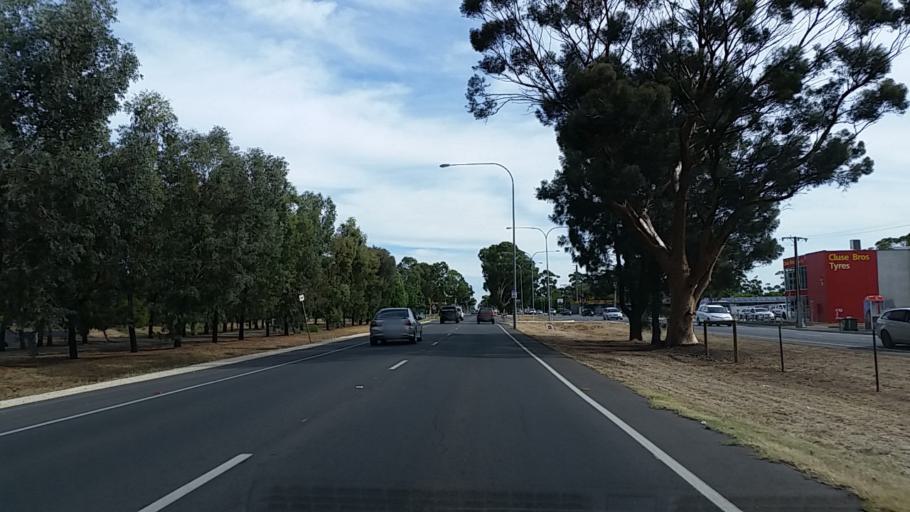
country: AU
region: South Australia
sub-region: Playford
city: Smithfield
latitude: -34.6817
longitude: 138.6946
